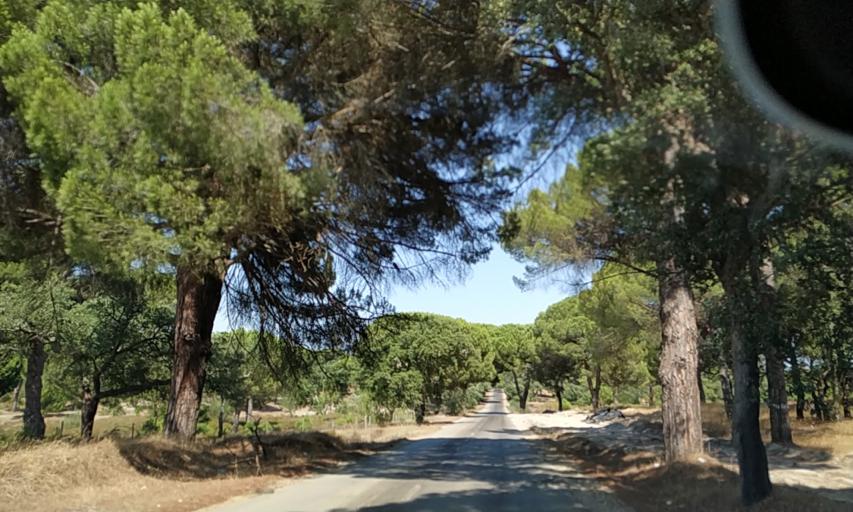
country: PT
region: Santarem
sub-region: Benavente
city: Poceirao
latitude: 38.7375
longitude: -8.6958
